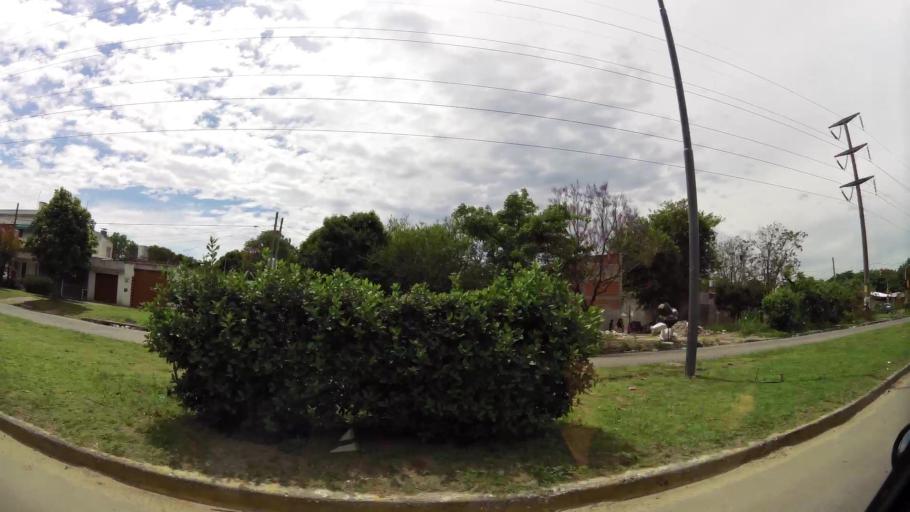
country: AR
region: Buenos Aires
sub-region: Partido de Quilmes
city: Quilmes
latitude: -34.7681
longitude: -58.2332
